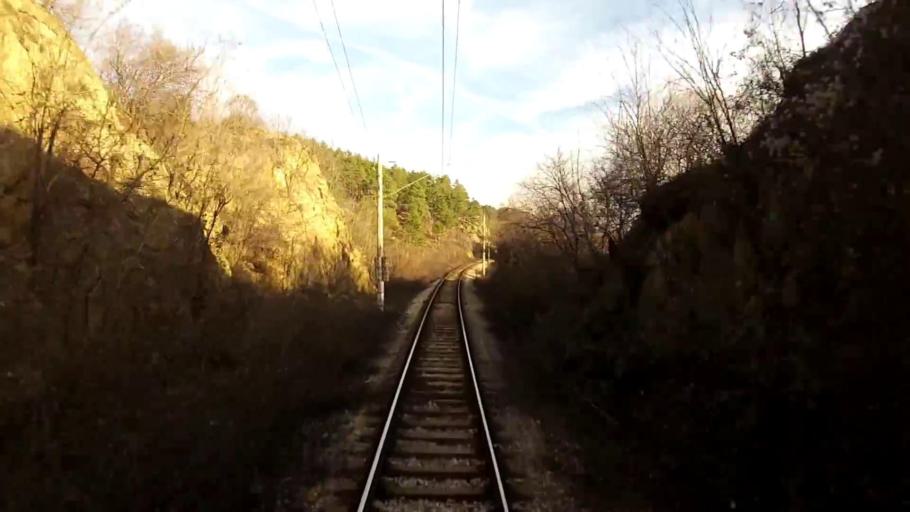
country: BG
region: Plovdiv
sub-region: Obshtina Karlovo
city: Klisura
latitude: 42.7202
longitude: 24.5964
